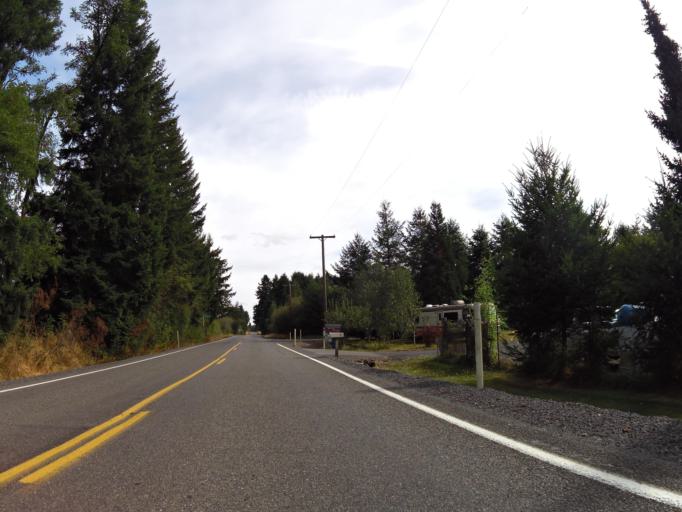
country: US
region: Washington
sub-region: Lewis County
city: Napavine
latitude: 46.5435
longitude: -122.9504
